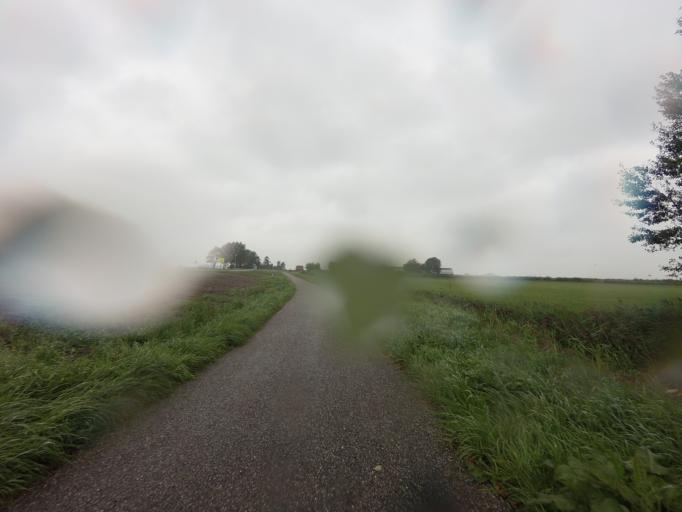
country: NL
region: Friesland
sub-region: Gemeente Boarnsterhim
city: Aldeboarn
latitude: 53.0553
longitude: 5.9230
